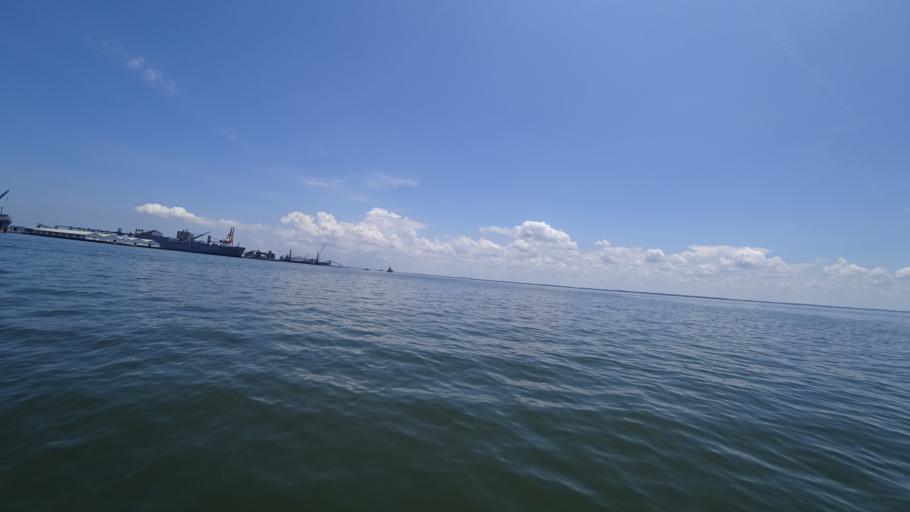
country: US
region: Virginia
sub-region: City of Newport News
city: Newport News
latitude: 36.9723
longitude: -76.4426
